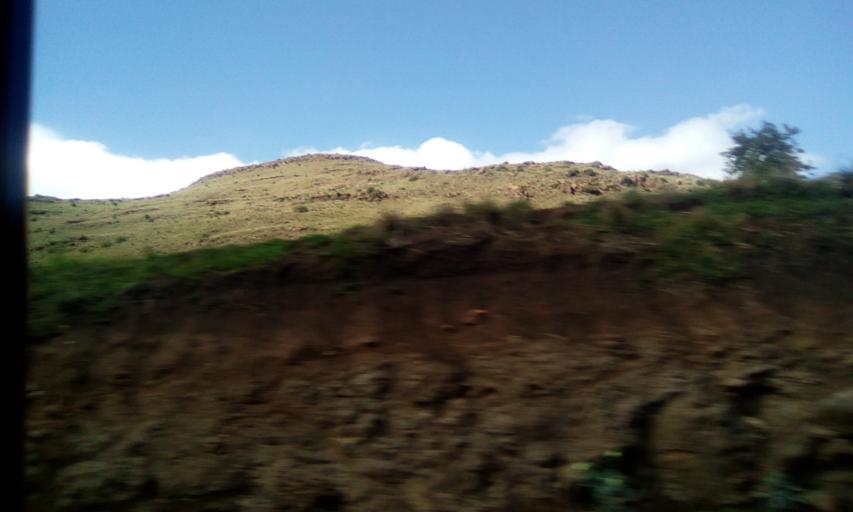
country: LS
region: Maseru
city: Nako
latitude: -29.6572
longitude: 27.8557
